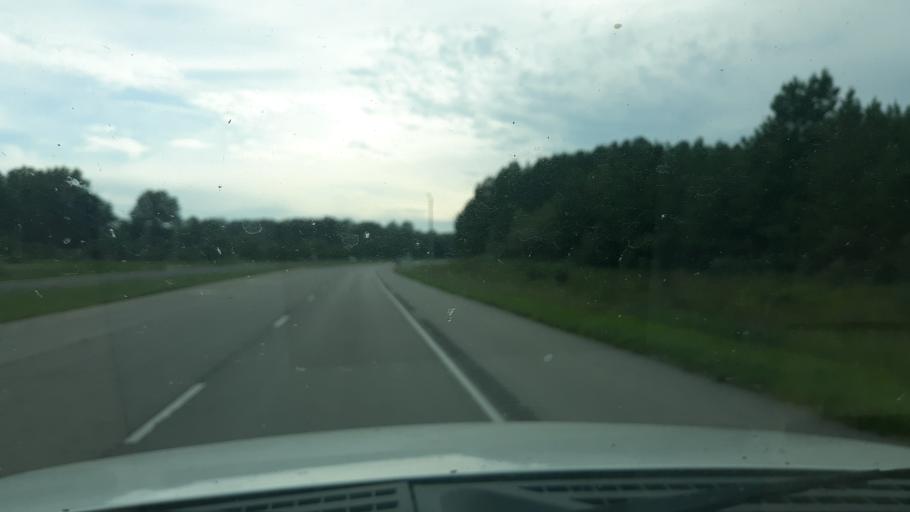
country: US
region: Illinois
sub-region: Williamson County
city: Marion
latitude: 37.7322
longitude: -88.8179
